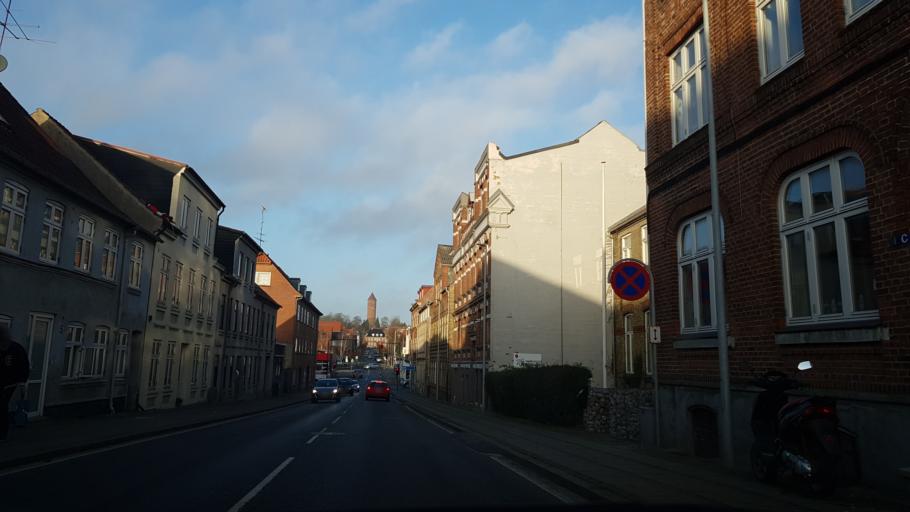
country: DK
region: South Denmark
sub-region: Haderslev Kommune
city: Haderslev
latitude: 55.2501
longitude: 9.4944
